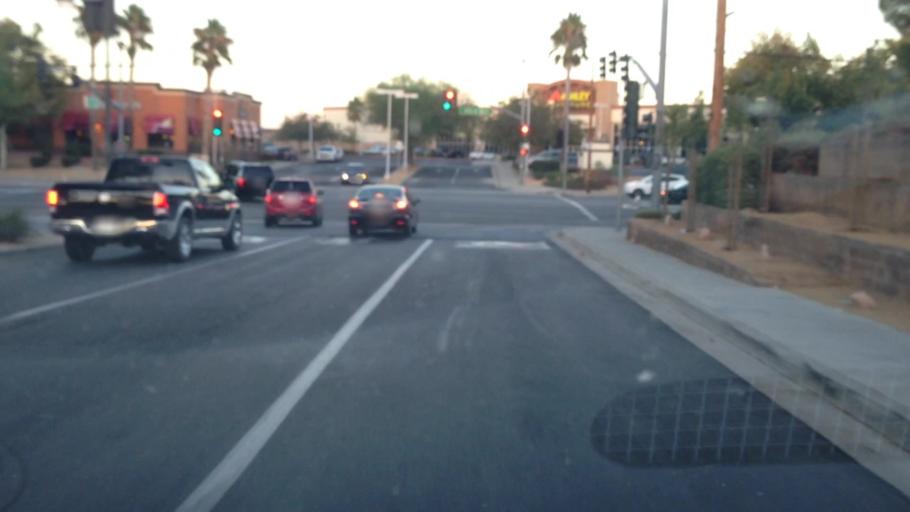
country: US
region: California
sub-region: Los Angeles County
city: Desert View Highlands
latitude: 34.6035
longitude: -118.1483
